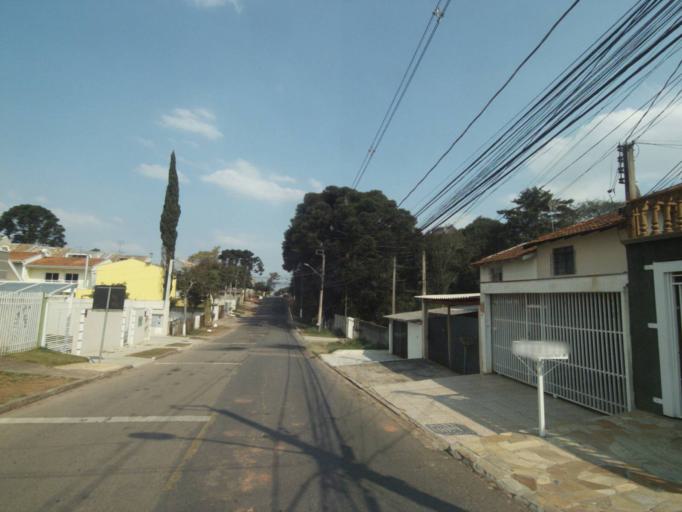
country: BR
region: Parana
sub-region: Sao Jose Dos Pinhais
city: Sao Jose dos Pinhais
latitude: -25.5132
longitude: -49.2493
